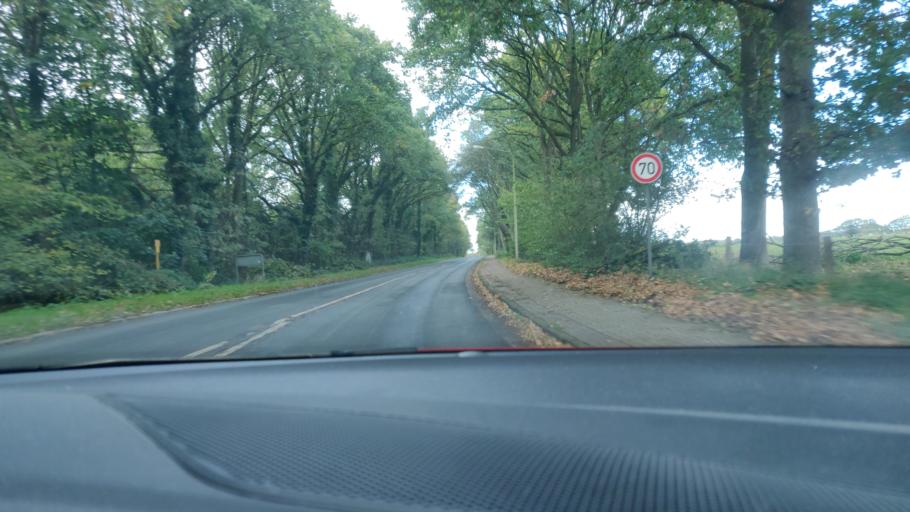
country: DE
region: Lower Saxony
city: Cuxhaven
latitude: 53.8499
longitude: 8.6394
